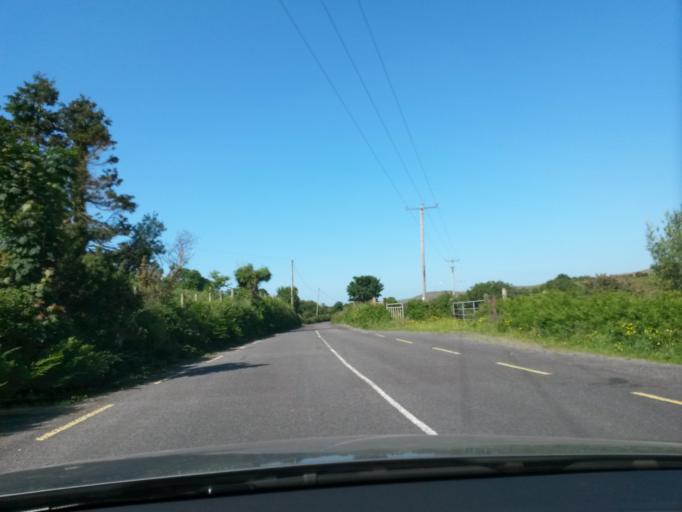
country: IE
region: Munster
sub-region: Ciarrai
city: Kenmare
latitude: 51.7400
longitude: -9.8751
